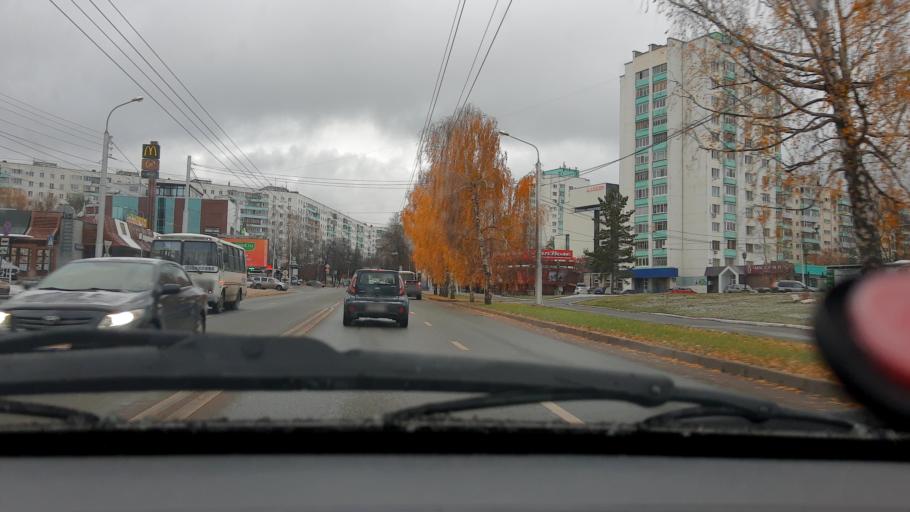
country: RU
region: Bashkortostan
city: Ufa
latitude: 54.7494
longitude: 56.0199
